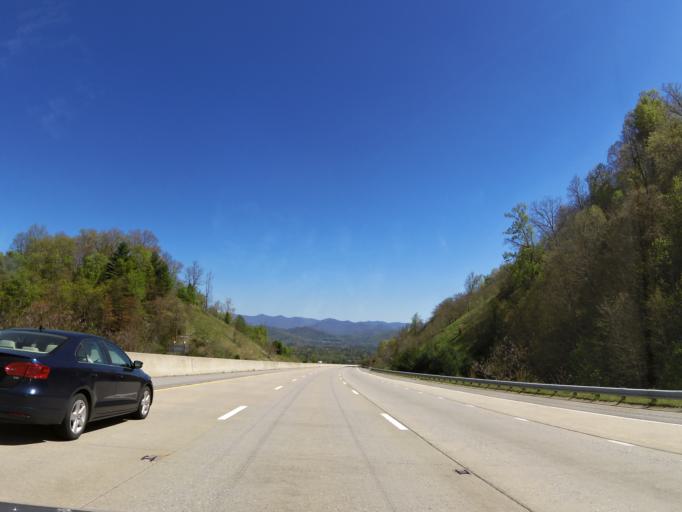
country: US
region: North Carolina
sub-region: Madison County
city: Mars Hill
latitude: 35.8707
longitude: -82.5383
